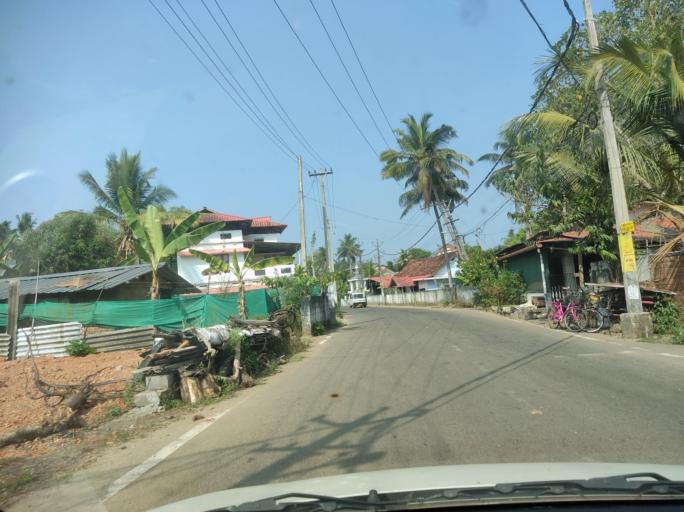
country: IN
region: Kerala
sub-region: Kottayam
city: Kottayam
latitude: 9.5778
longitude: 76.5016
